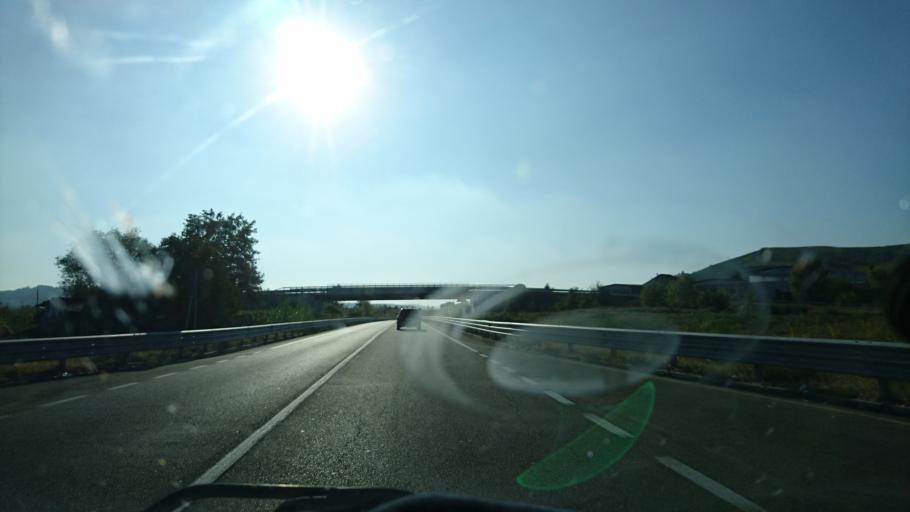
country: IT
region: Piedmont
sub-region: Provincia di Alessandria
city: Strevi
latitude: 44.6850
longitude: 8.5186
